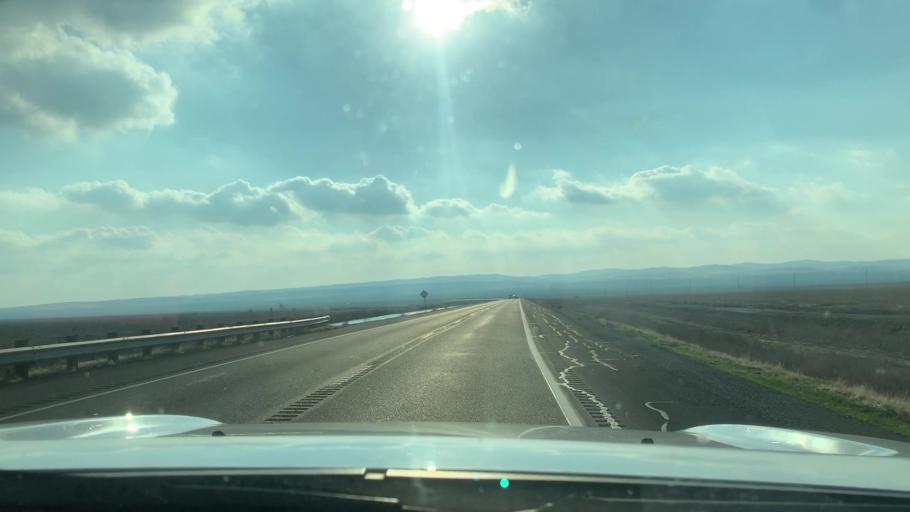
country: US
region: California
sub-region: Kings County
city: Kettleman City
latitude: 36.0480
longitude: -119.9466
